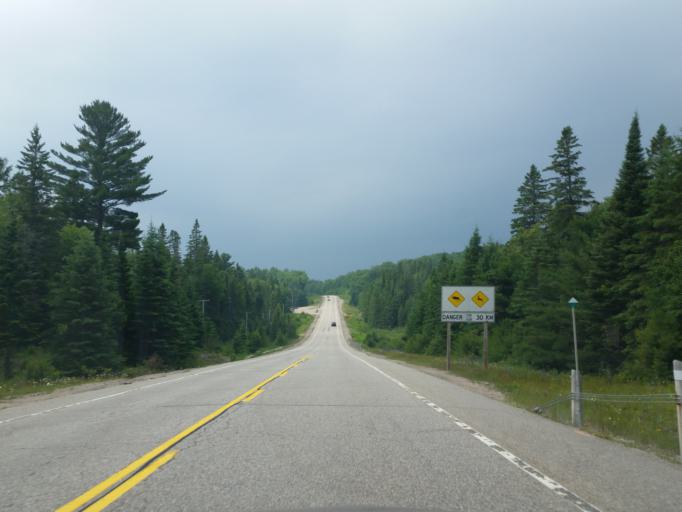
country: CA
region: Ontario
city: Huntsville
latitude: 45.5622
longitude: -78.5725
